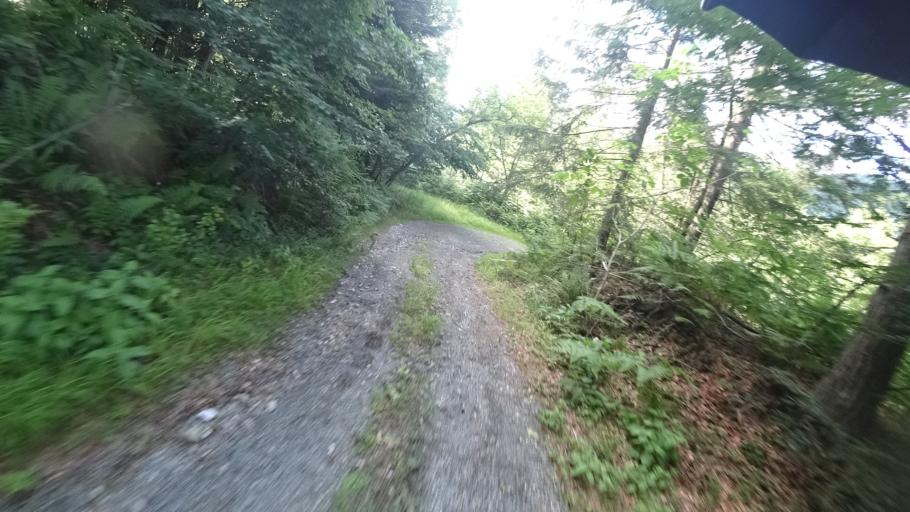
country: SI
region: Osilnica
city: Osilnica
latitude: 45.4719
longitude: 14.7027
